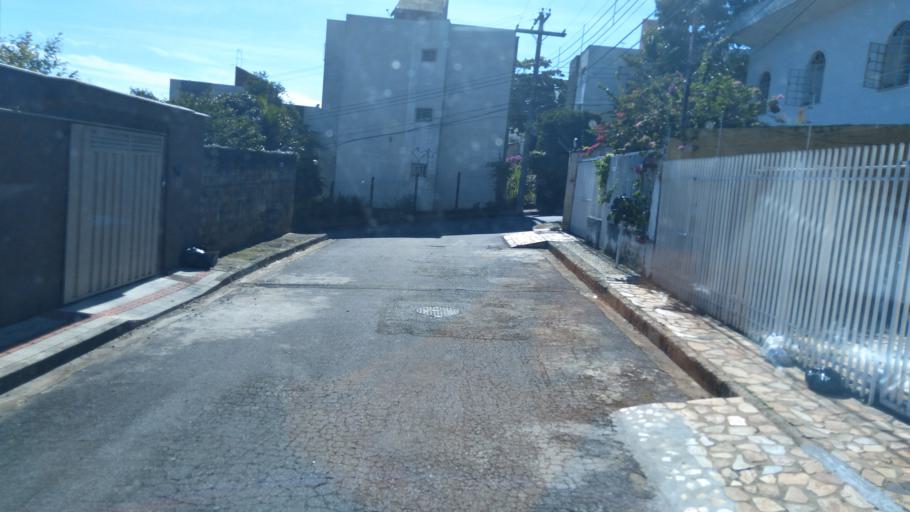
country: BR
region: Minas Gerais
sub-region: Contagem
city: Contagem
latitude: -19.9208
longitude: -44.0071
